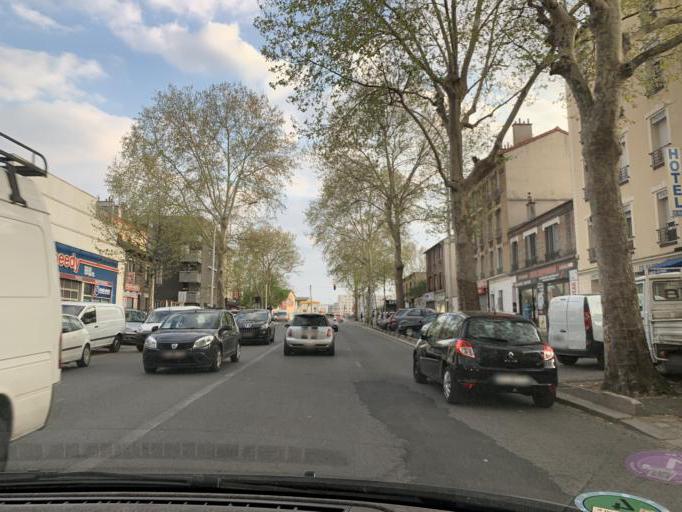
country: FR
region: Ile-de-France
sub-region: Departement de Seine-Saint-Denis
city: Aubervilliers
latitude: 48.9099
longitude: 2.3788
